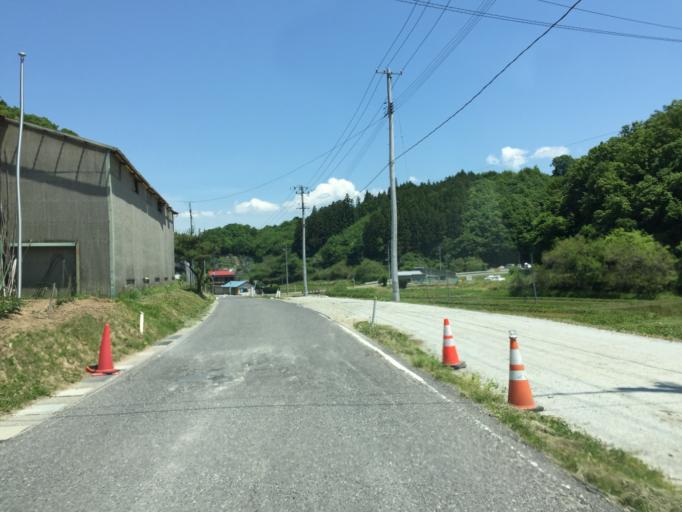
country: JP
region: Fukushima
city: Funehikimachi-funehiki
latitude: 37.4876
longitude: 140.5455
